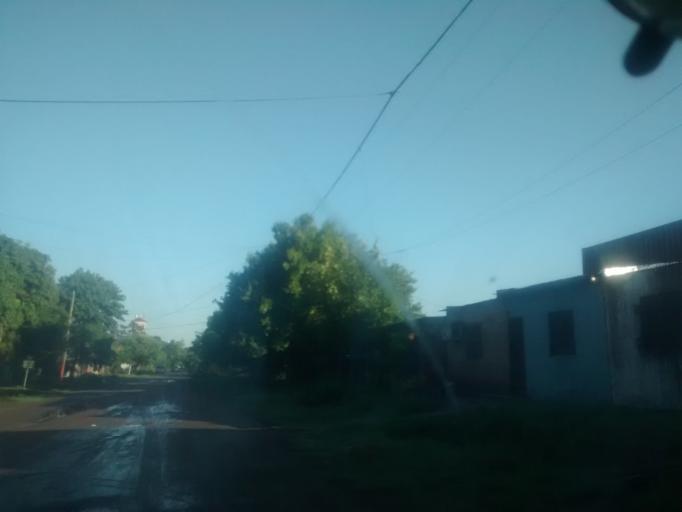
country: AR
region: Chaco
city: Resistencia
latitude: -27.4680
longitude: -58.9778
